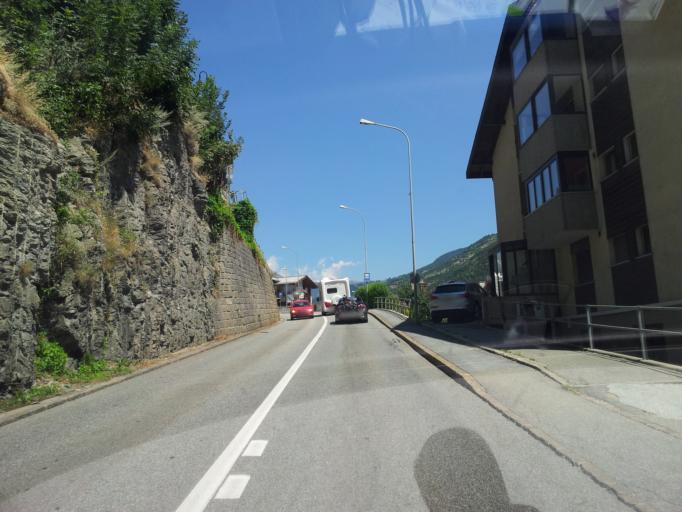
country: CH
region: Valais
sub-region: Visp District
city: Stalden
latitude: 46.2315
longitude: 7.8692
